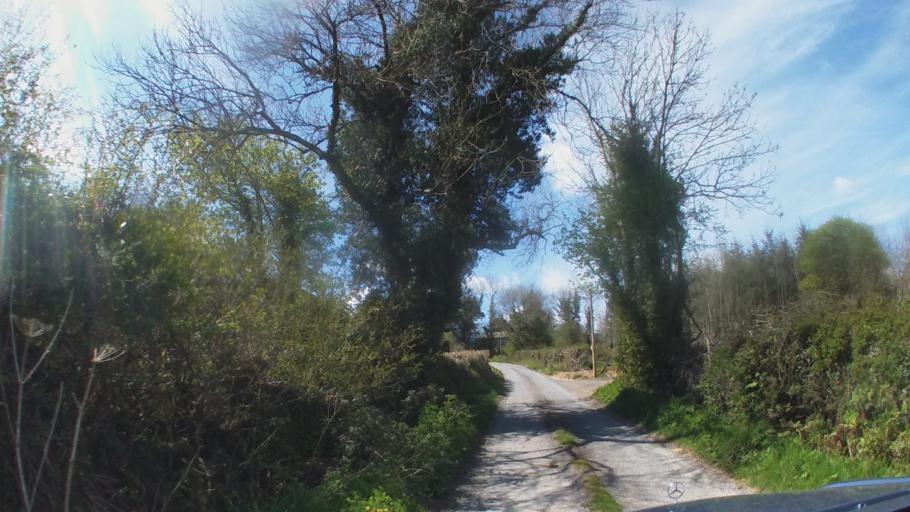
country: IE
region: Leinster
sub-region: Kilkenny
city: Callan
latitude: 52.6212
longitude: -7.5081
